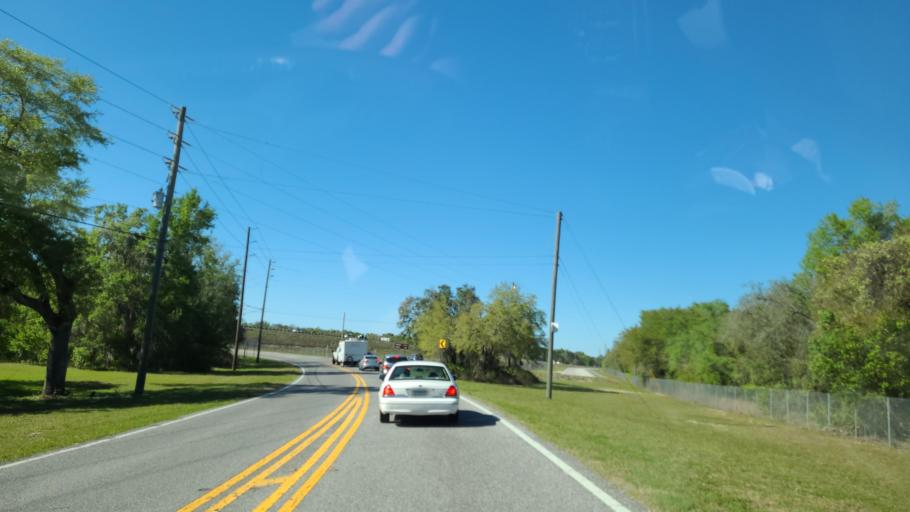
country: US
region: Florida
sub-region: Pasco County
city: Shady Hills
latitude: 28.3701
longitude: -82.5420
